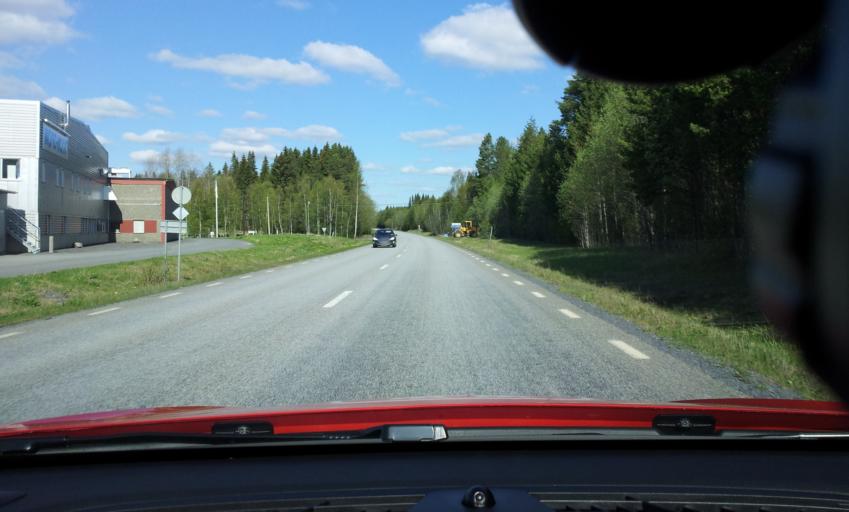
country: SE
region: Jaemtland
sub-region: Krokoms Kommun
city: Valla
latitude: 63.2680
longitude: 13.9604
